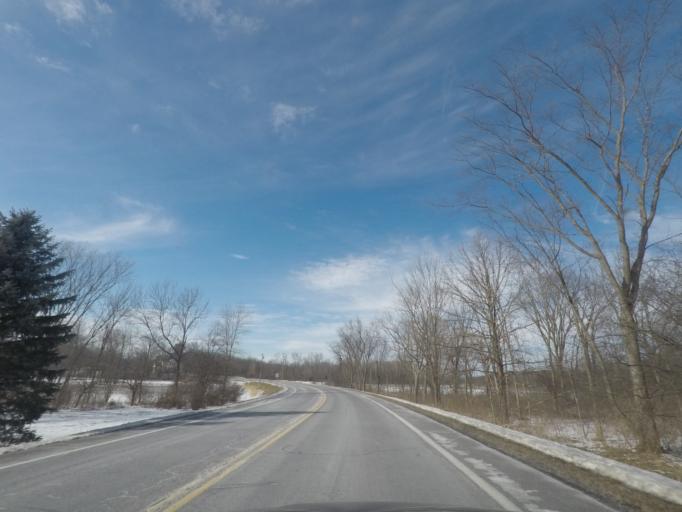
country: US
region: New York
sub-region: Albany County
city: Voorheesville
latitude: 42.6749
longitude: -73.9445
